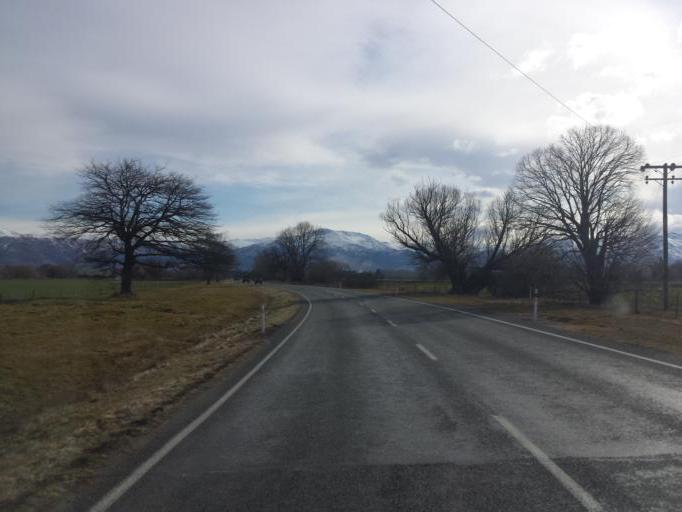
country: NZ
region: Canterbury
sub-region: Timaru District
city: Pleasant Point
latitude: -44.0857
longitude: 170.8135
